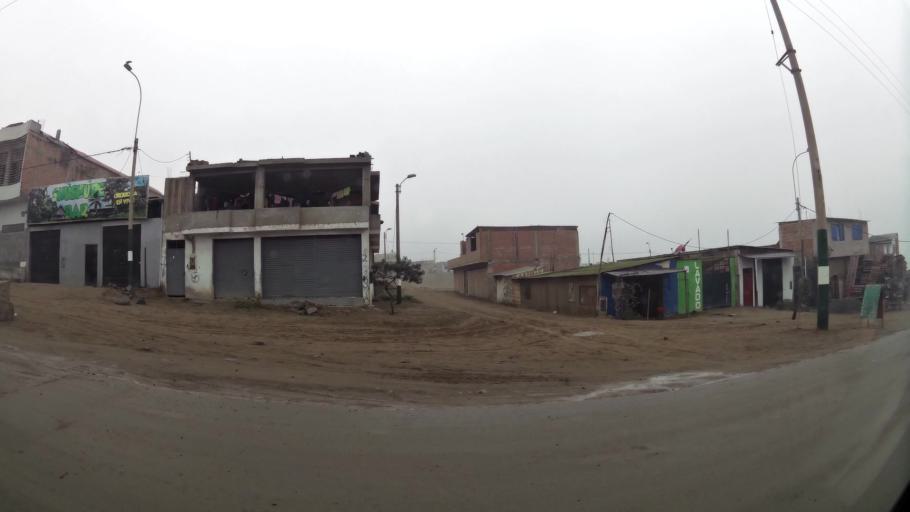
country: PE
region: Lima
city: Ventanilla
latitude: -11.8387
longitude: -77.1400
